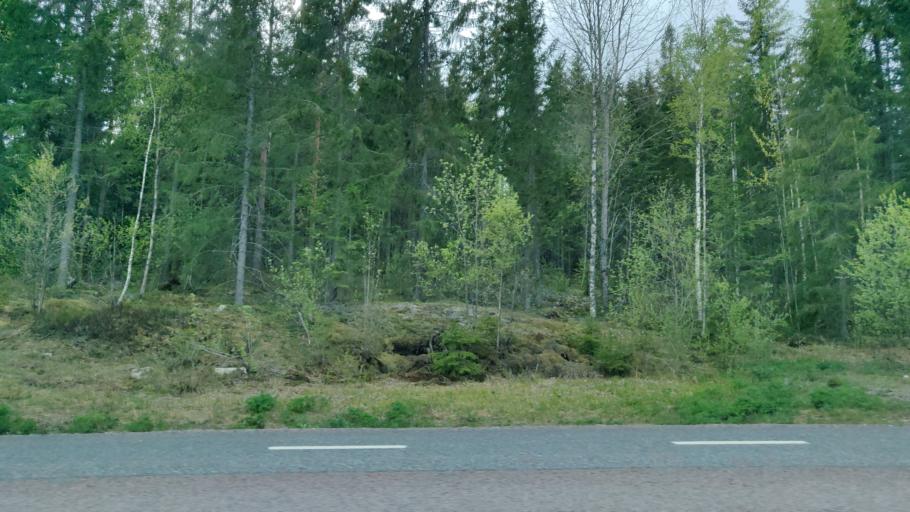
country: SE
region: Vaermland
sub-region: Forshaga Kommun
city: Deje
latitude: 59.6554
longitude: 13.4384
